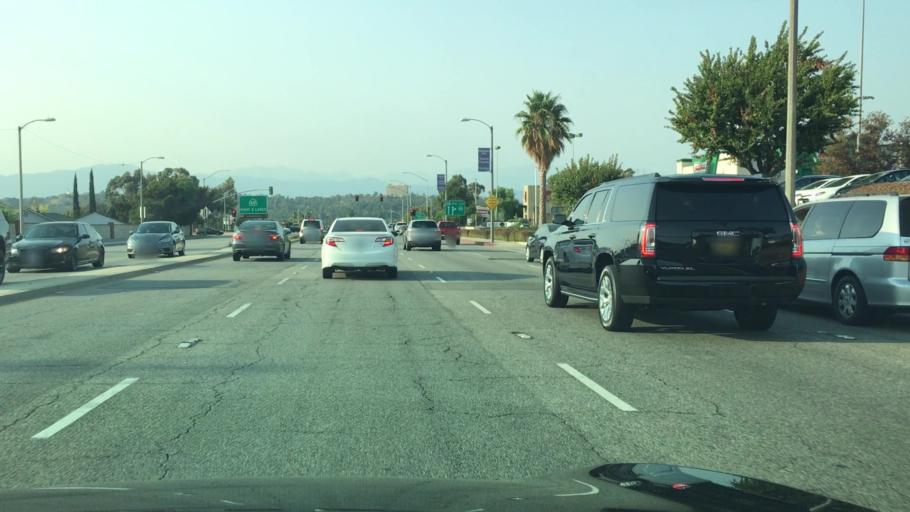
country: US
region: California
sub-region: Los Angeles County
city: La Puente
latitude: 33.9943
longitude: -117.9314
